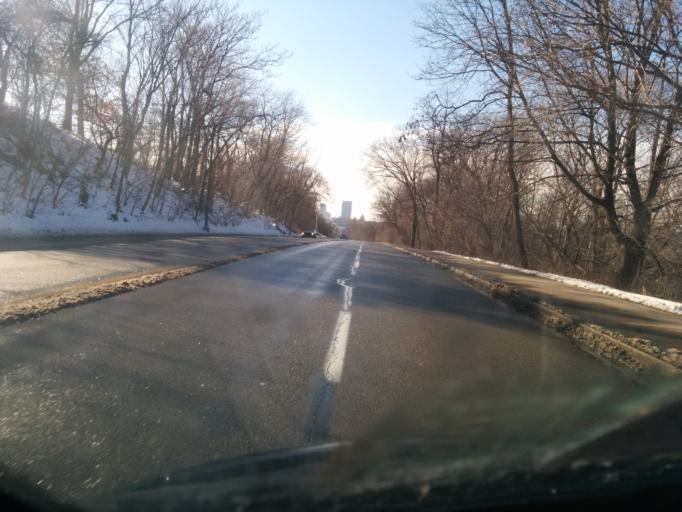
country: US
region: Pennsylvania
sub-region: Allegheny County
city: Bloomfield
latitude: 40.4341
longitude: -79.9398
